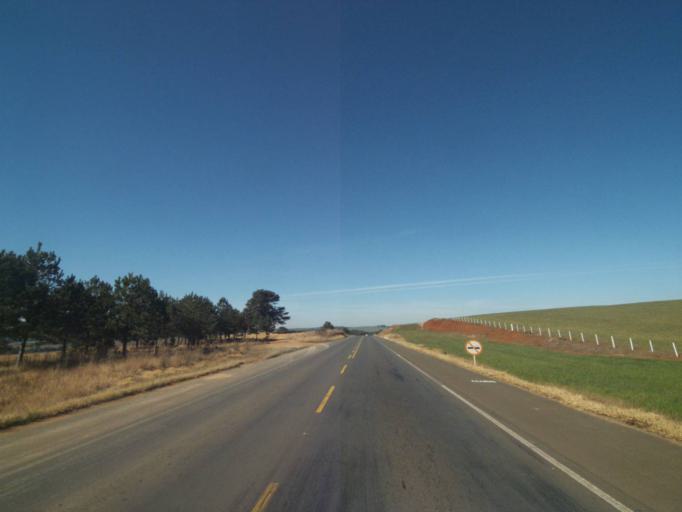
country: BR
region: Parana
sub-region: Tibagi
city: Tibagi
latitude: -24.6430
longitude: -50.4558
